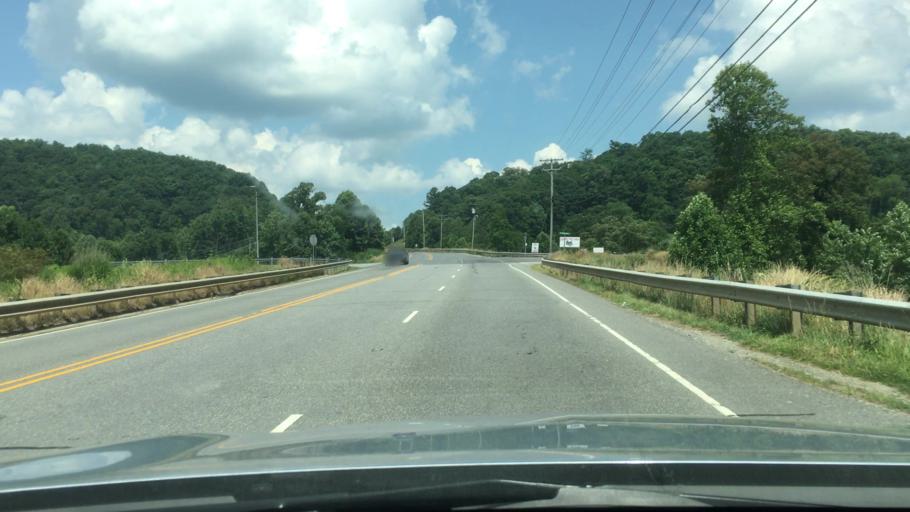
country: US
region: North Carolina
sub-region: Madison County
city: Marshall
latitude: 35.8195
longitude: -82.6425
